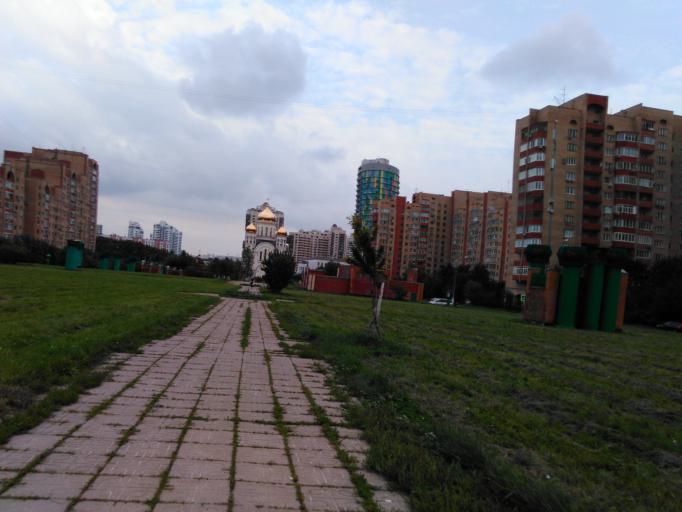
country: RU
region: Moskovskaya
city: Cheremushki
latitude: 55.6683
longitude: 37.5577
